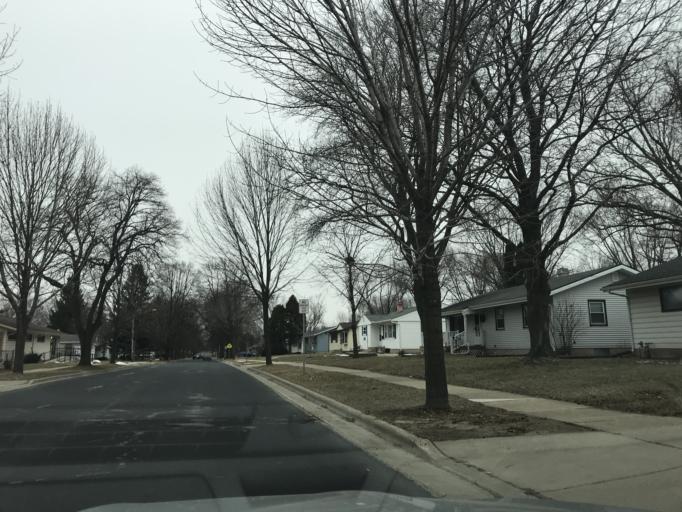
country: US
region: Wisconsin
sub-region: Dane County
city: Monona
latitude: 43.0929
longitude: -89.3022
